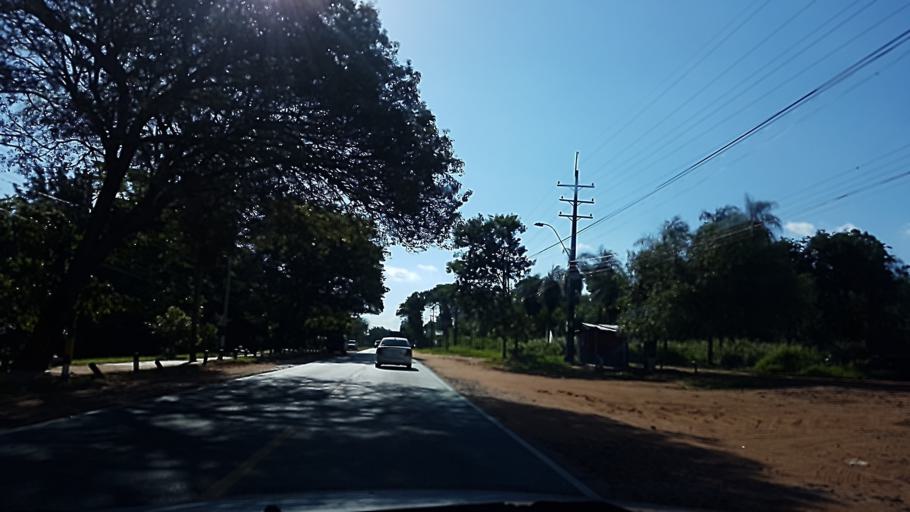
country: PY
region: Central
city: San Antonio
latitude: -25.4479
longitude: -57.5251
